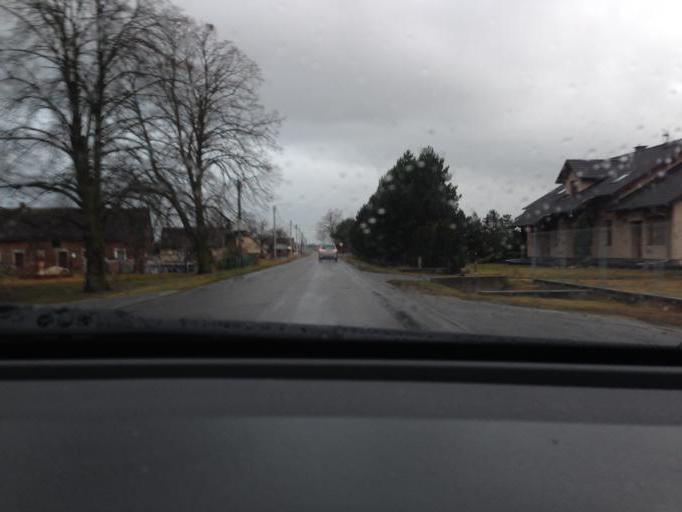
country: PL
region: Opole Voivodeship
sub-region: Powiat opolski
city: Wegry
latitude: 50.7208
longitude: 18.0124
